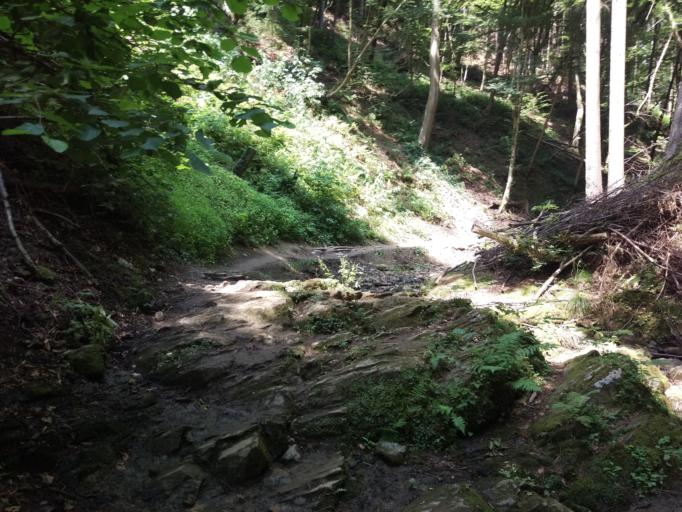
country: AT
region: Styria
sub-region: Graz Stadt
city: Mariatrost
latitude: 47.1089
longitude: 15.4781
